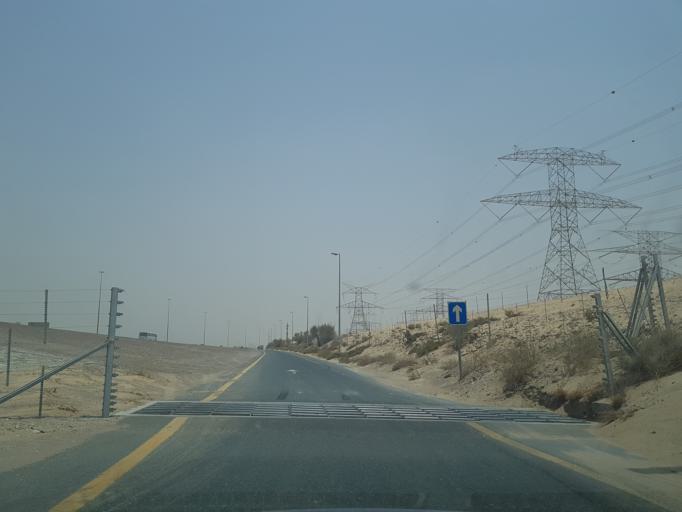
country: AE
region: Dubai
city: Dubai
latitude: 25.0596
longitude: 55.3233
